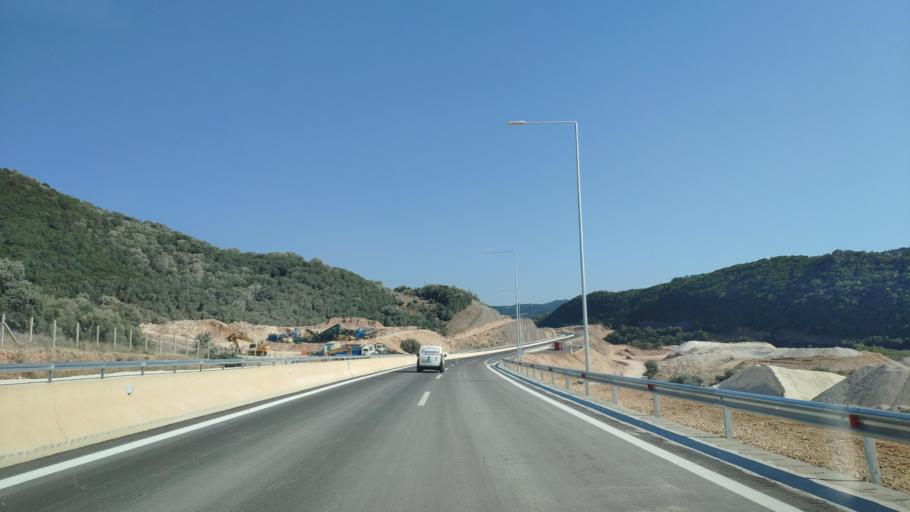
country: GR
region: West Greece
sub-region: Nomos Aitolias kai Akarnanias
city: Katouna
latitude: 38.7920
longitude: 21.1411
